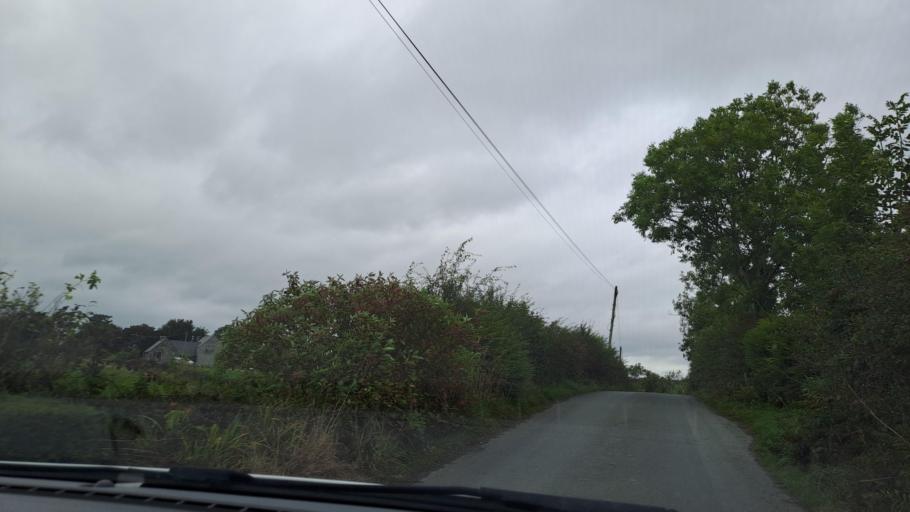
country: IE
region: Ulster
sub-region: An Cabhan
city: Kingscourt
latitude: 54.0095
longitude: -6.8576
